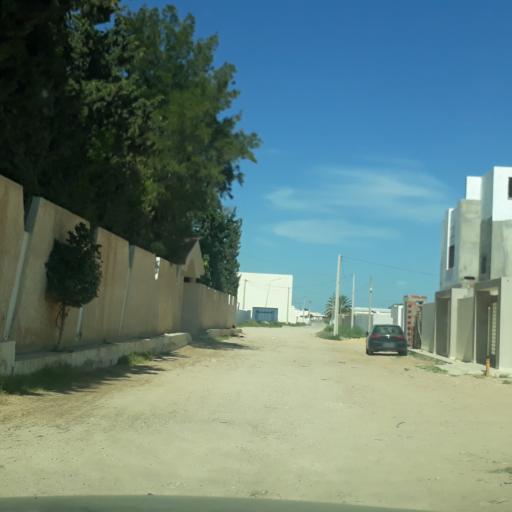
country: TN
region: Safaqis
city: Al Qarmadah
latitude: 34.8316
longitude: 10.7609
